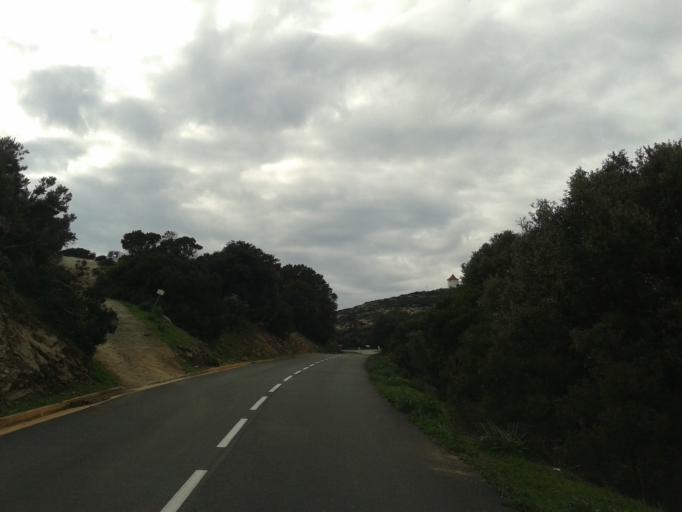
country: FR
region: Corsica
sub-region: Departement de la Haute-Corse
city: Brando
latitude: 42.9732
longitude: 9.3690
